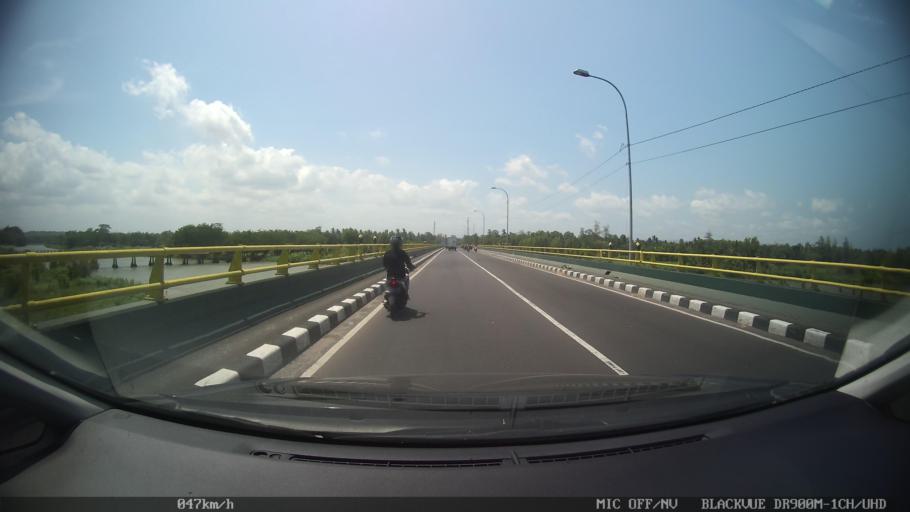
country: ID
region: Daerah Istimewa Yogyakarta
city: Srandakan
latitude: -7.9395
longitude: 110.2415
